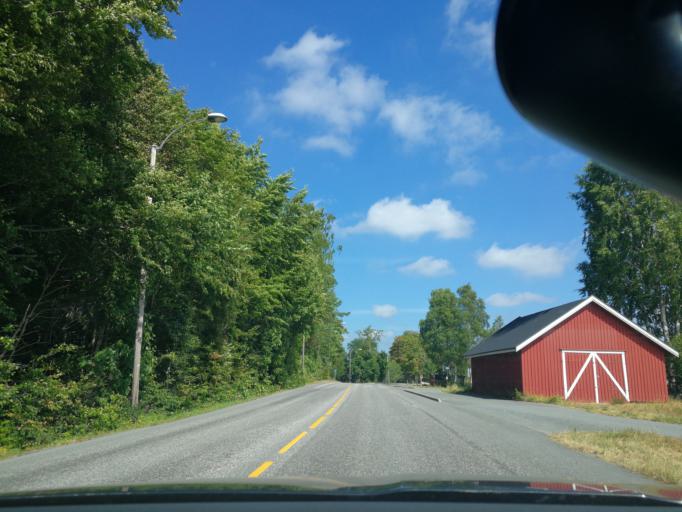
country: NO
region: Vestfold
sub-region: Sandefjord
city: Sandefjord
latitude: 59.1582
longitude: 10.1997
